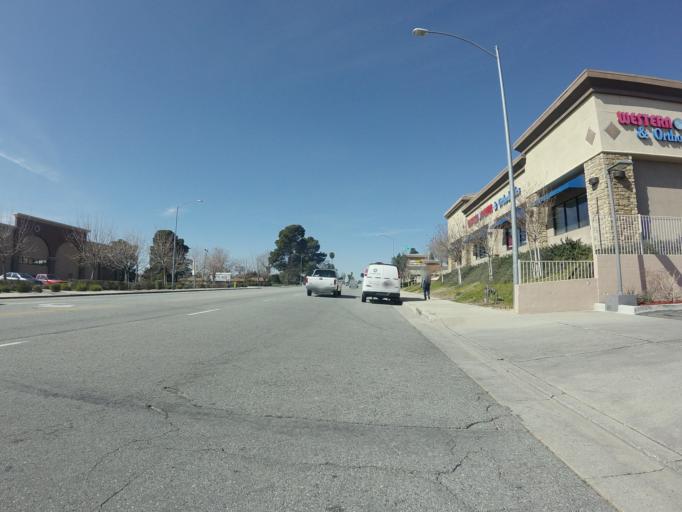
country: US
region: California
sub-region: Riverside County
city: Banning
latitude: 33.9255
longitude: -116.8859
